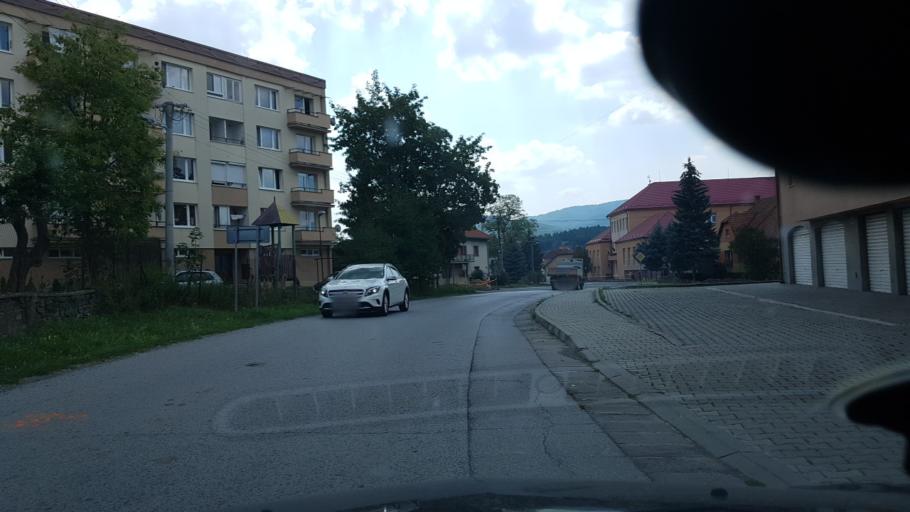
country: SK
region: Banskobystricky
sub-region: Okres Banska Bystrica
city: Zvolen
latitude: 48.5629
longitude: 19.2580
